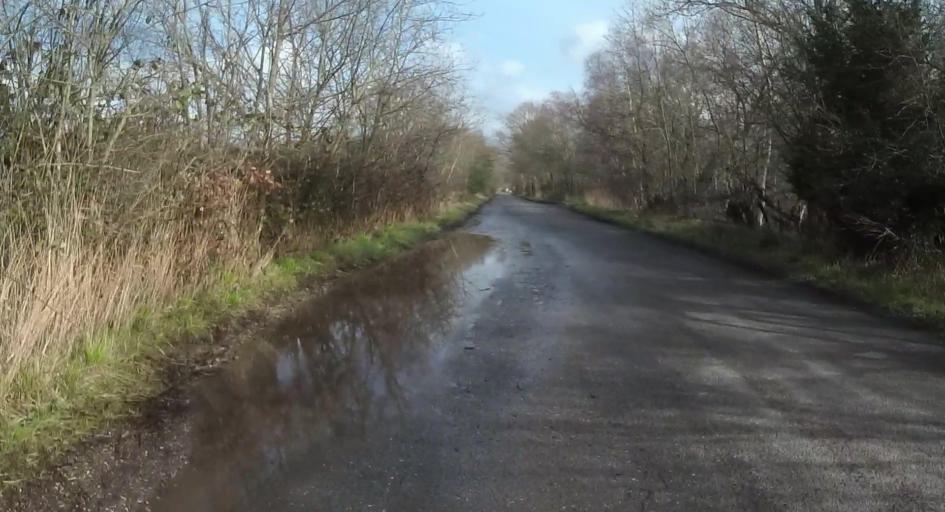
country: GB
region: England
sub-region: West Berkshire
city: Thatcham
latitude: 51.3781
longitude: -1.2524
